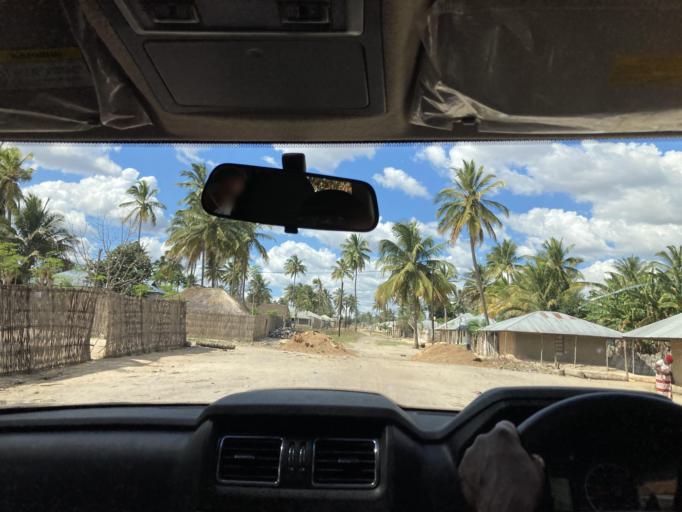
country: MZ
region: Cabo Delgado
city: Montepuez
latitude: -13.1299
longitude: 39.0112
